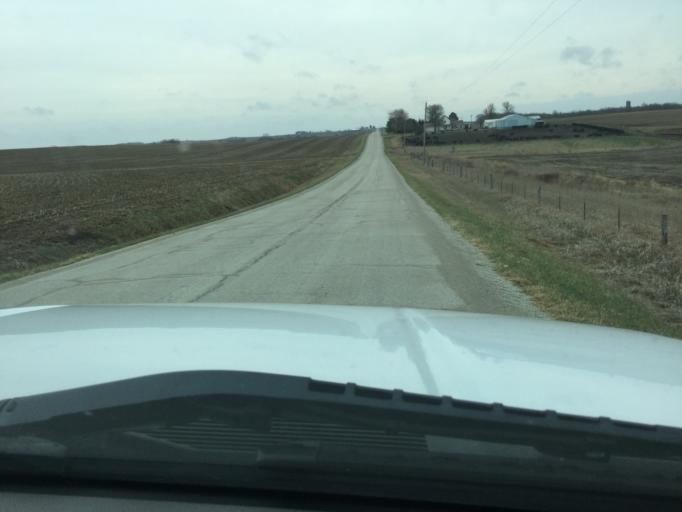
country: US
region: Kansas
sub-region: Nemaha County
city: Sabetha
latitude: 39.8414
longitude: -95.7142
